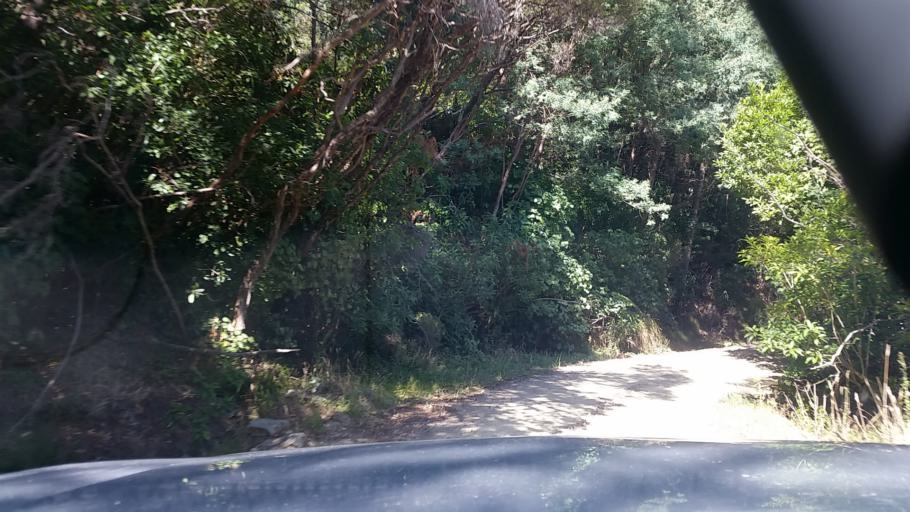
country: NZ
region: Marlborough
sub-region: Marlborough District
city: Picton
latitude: -41.3048
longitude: 174.1775
